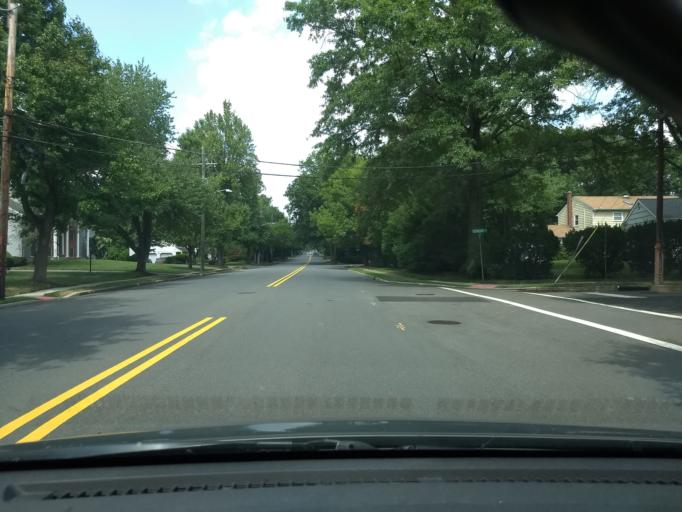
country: US
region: New Jersey
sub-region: Bergen County
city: Ho-Ho-Kus
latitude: 40.9770
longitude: -74.0892
